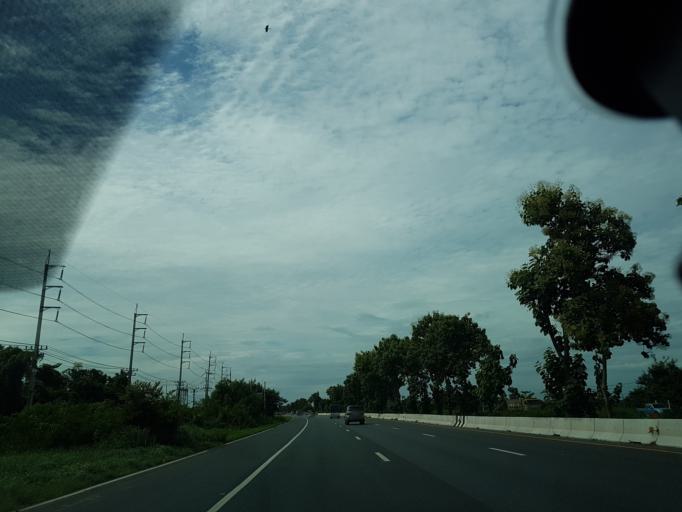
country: TH
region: Ang Thong
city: Chaiyo
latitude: 14.6944
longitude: 100.4585
